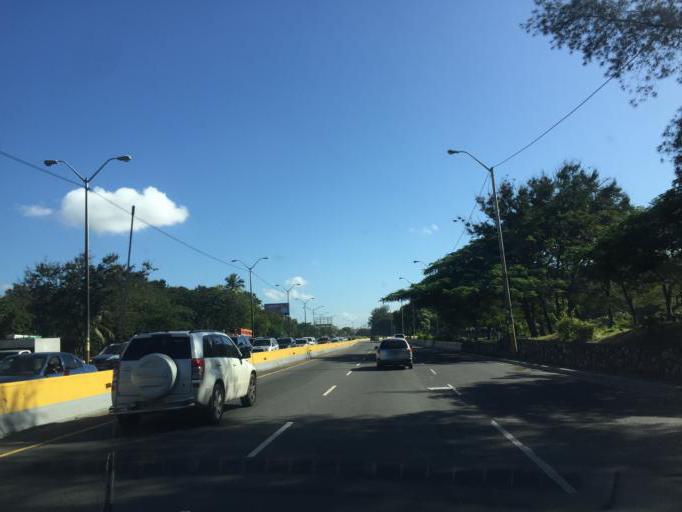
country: DO
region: Santo Domingo
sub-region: Santo Domingo
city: Santo Domingo Este
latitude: 18.4845
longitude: -69.8551
